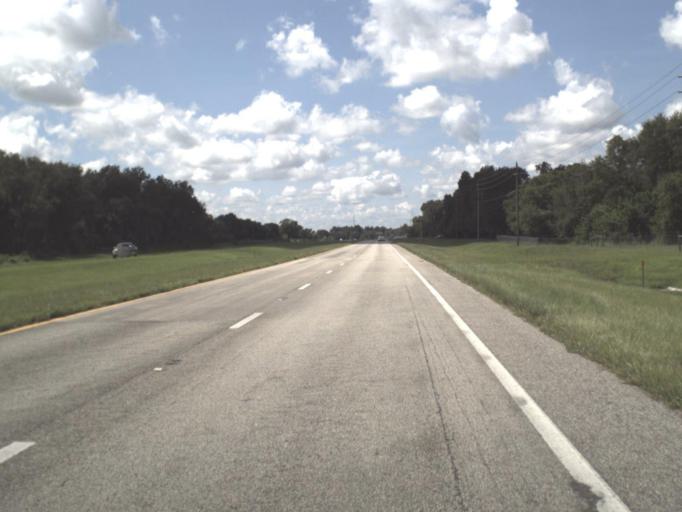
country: US
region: Florida
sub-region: DeSoto County
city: Arcadia
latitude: 27.2552
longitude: -81.8432
